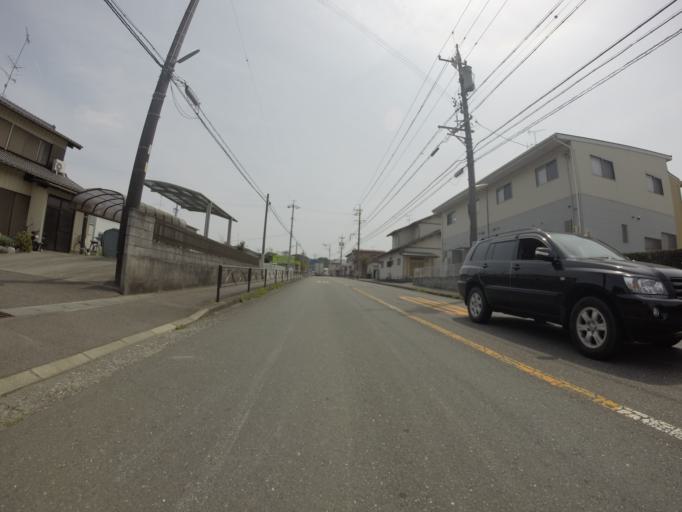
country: JP
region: Shizuoka
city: Kakegawa
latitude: 34.7666
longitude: 138.0294
